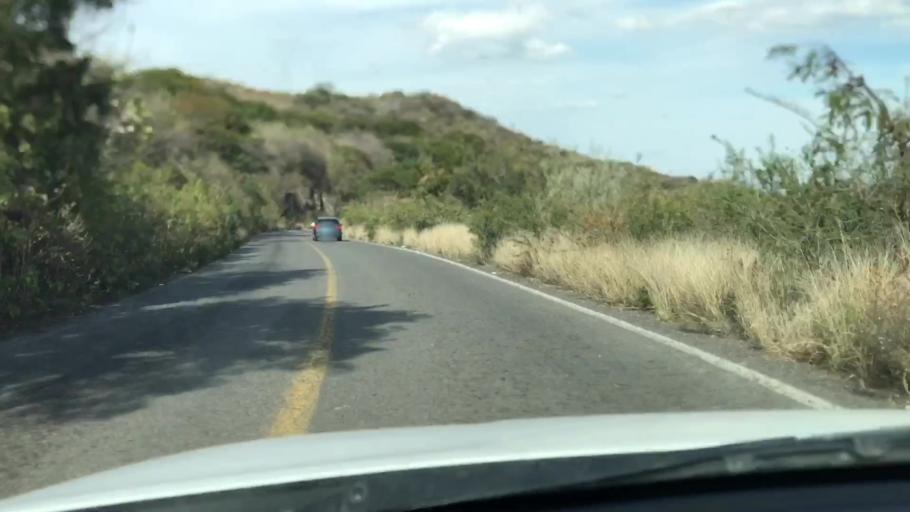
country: MX
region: Jalisco
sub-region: Zacoalco de Torres
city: Barranca de Otates (Barranca de Otatan)
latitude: 20.2396
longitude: -103.6843
